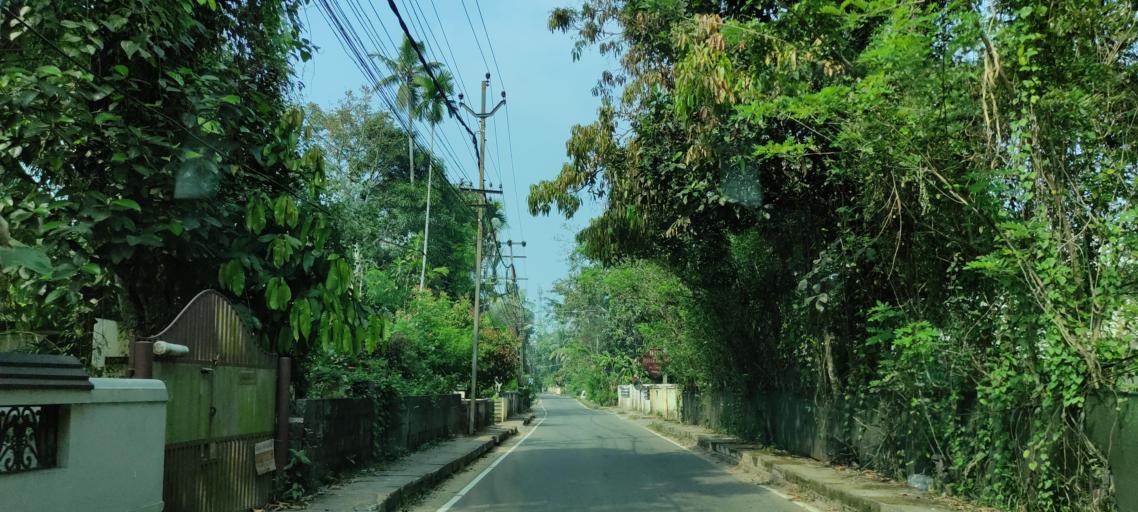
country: IN
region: Kerala
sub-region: Kottayam
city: Vaikam
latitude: 9.7471
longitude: 76.4019
